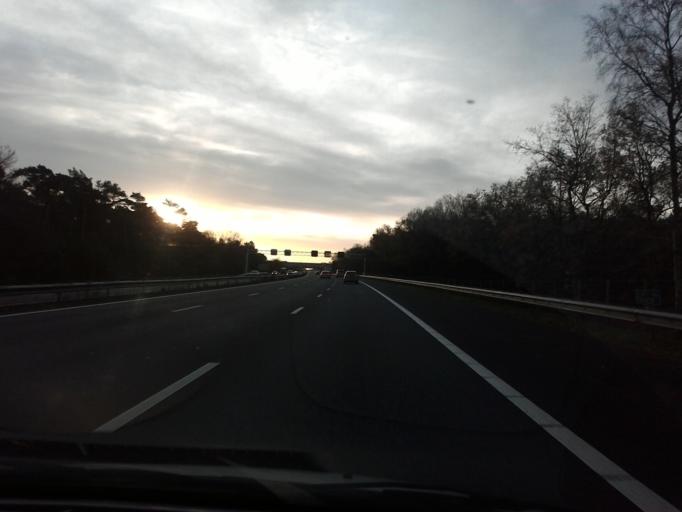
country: NL
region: North Brabant
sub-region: Gemeente Eindhoven
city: De Doornakkers
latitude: 51.3817
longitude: 5.5128
